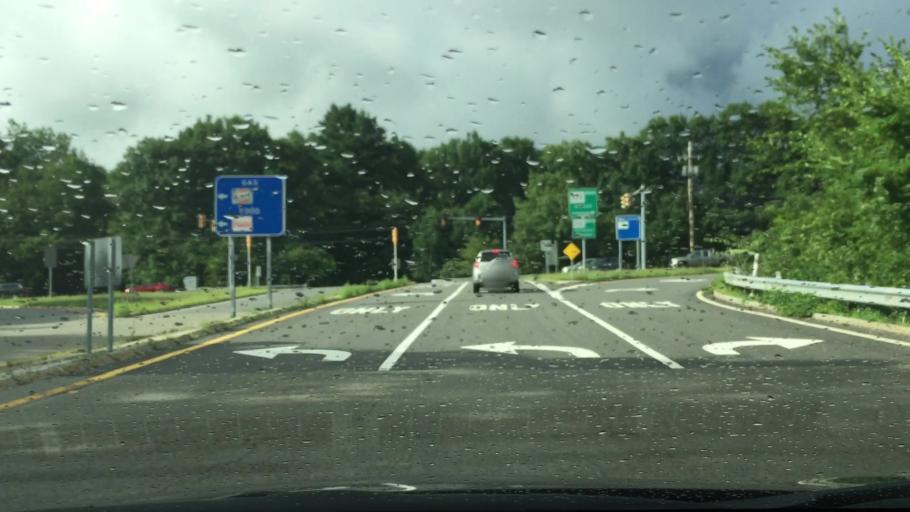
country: US
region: Massachusetts
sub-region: Worcester County
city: Harvard
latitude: 42.4870
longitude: -71.5421
